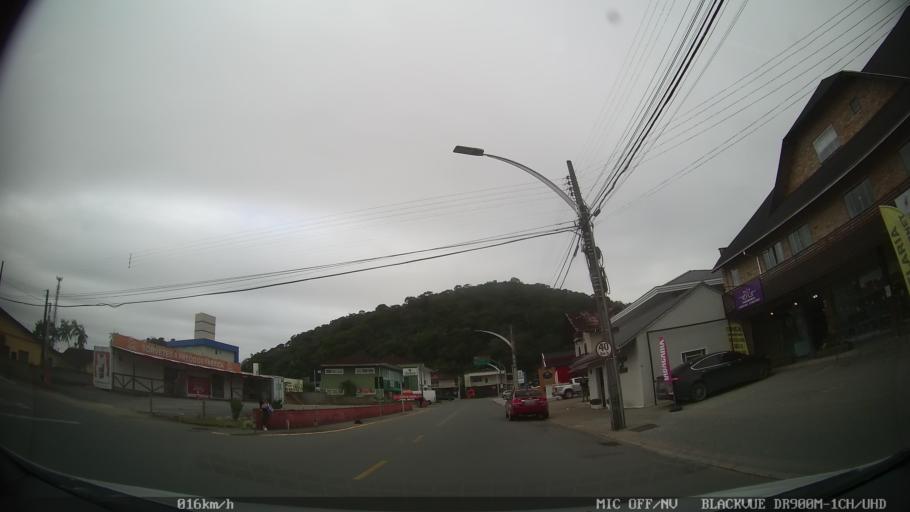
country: BR
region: Santa Catarina
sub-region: Joinville
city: Joinville
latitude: -26.2099
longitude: -48.9085
